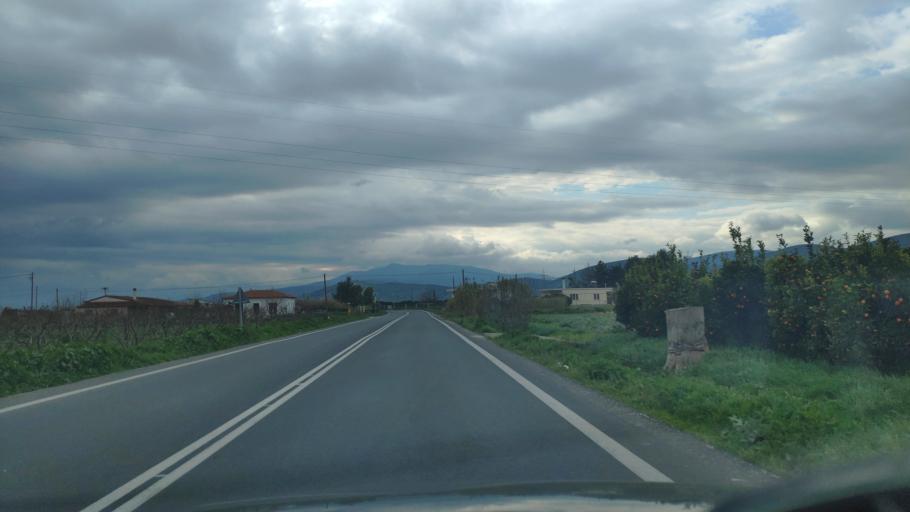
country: GR
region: Peloponnese
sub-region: Nomos Argolidos
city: Nea Kios
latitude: 37.5921
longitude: 22.7083
